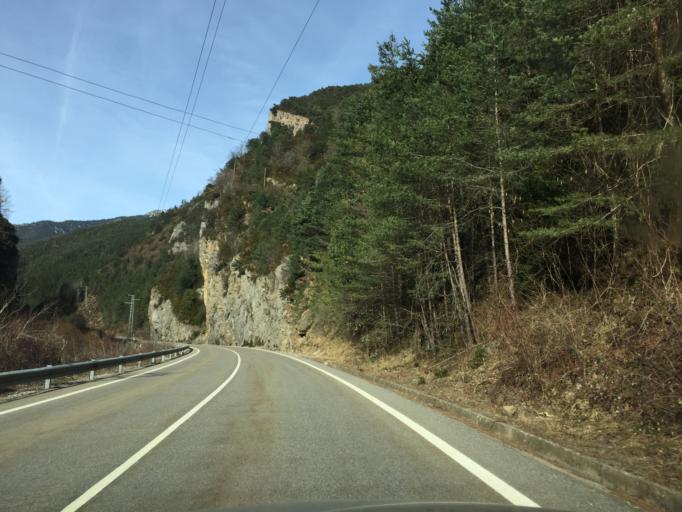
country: ES
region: Aragon
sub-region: Provincia de Huesca
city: Bielsa
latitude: 42.6004
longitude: 0.2401
